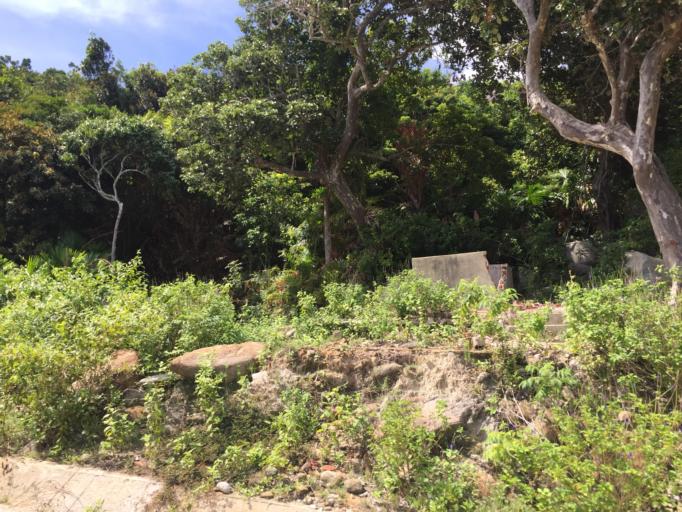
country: VN
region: Quang Nam
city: Hoi An
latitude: 15.9637
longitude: 108.5102
